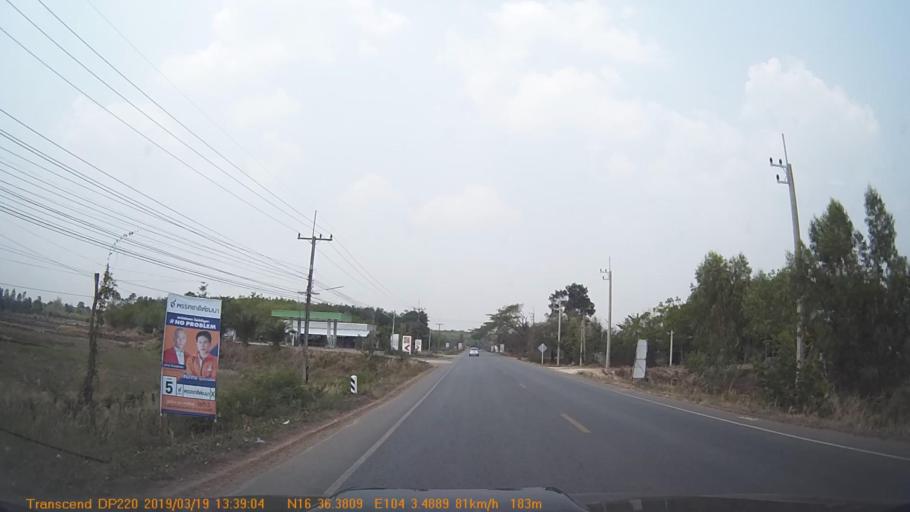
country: TH
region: Kalasin
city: Kuchinarai
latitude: 16.6068
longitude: 104.0582
